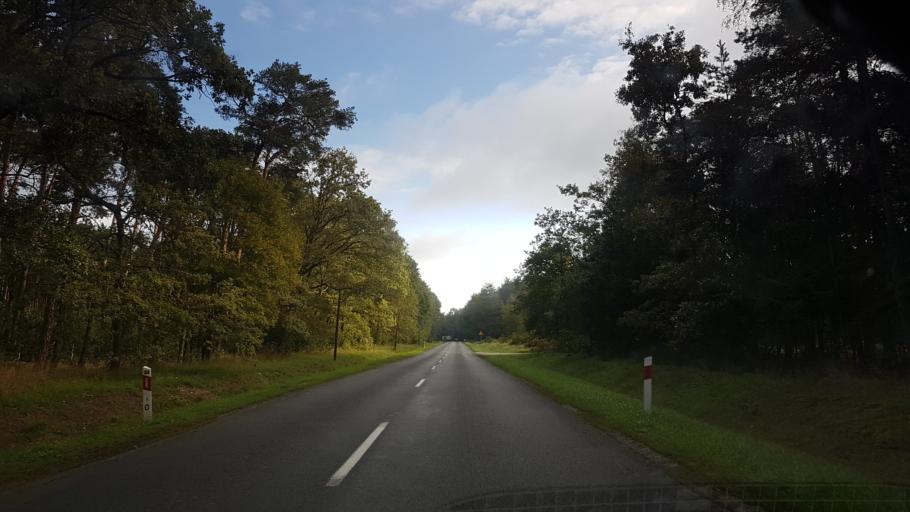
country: PL
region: Greater Poland Voivodeship
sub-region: Leszno
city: Leszno
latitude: 51.7994
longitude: 16.5764
